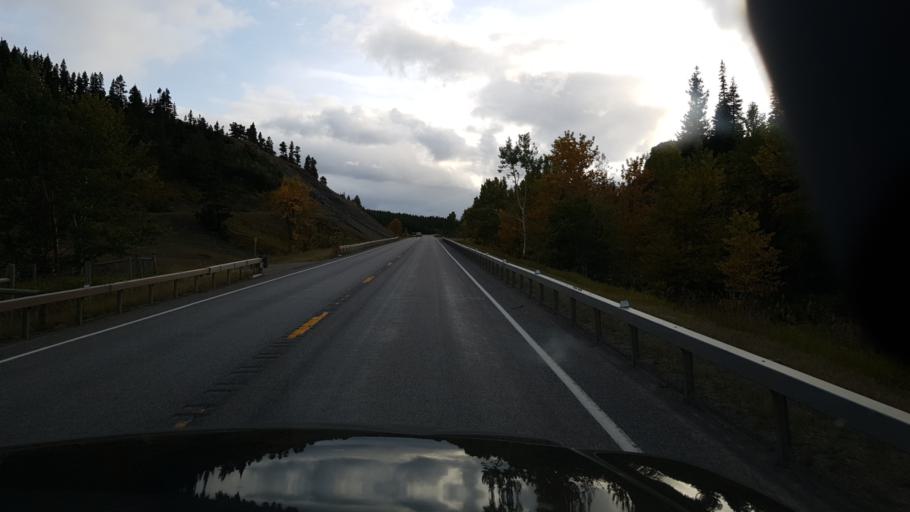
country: US
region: Montana
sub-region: Glacier County
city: South Browning
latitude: 48.3972
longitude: -113.2542
